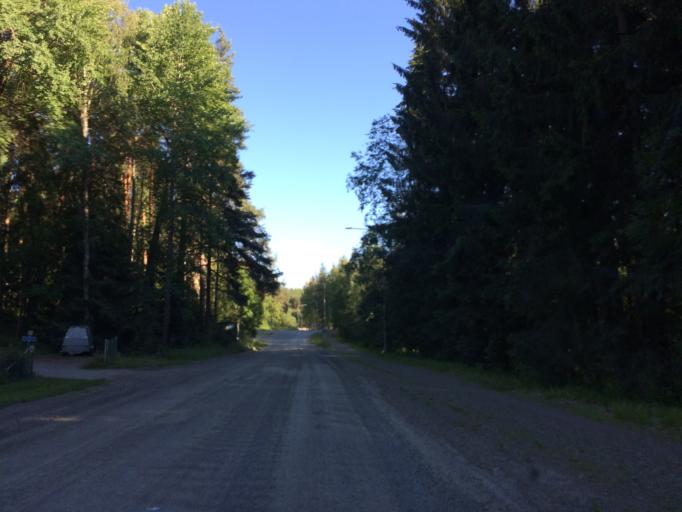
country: FI
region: Haeme
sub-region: Haemeenlinna
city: Haemeenlinna
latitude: 60.9874
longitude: 24.5063
